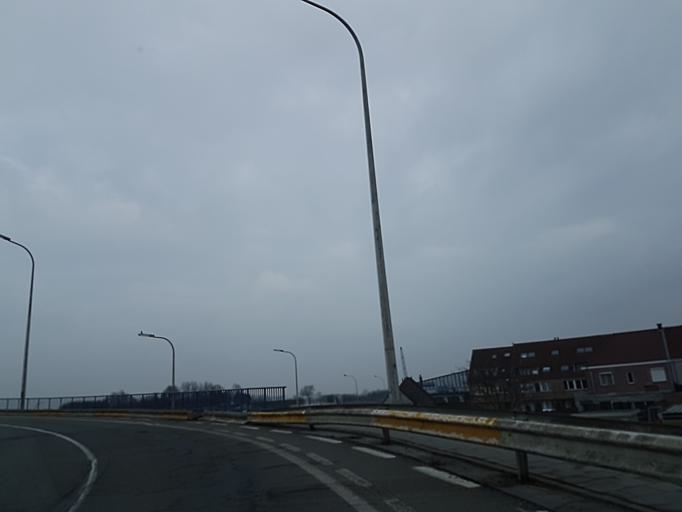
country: BE
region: Flanders
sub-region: Provincie Oost-Vlaanderen
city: Deinze
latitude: 50.9887
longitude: 3.5248
